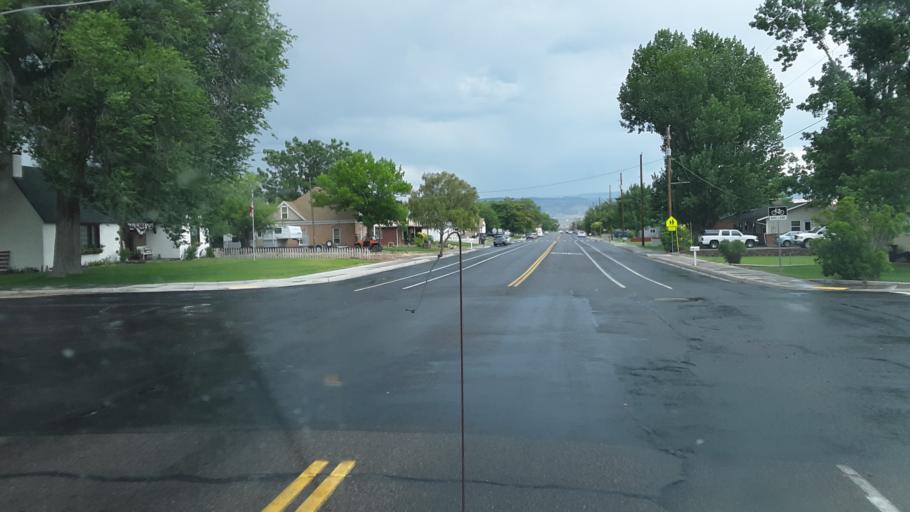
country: US
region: Utah
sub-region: Sevier County
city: Richfield
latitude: 38.7723
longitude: -112.0904
